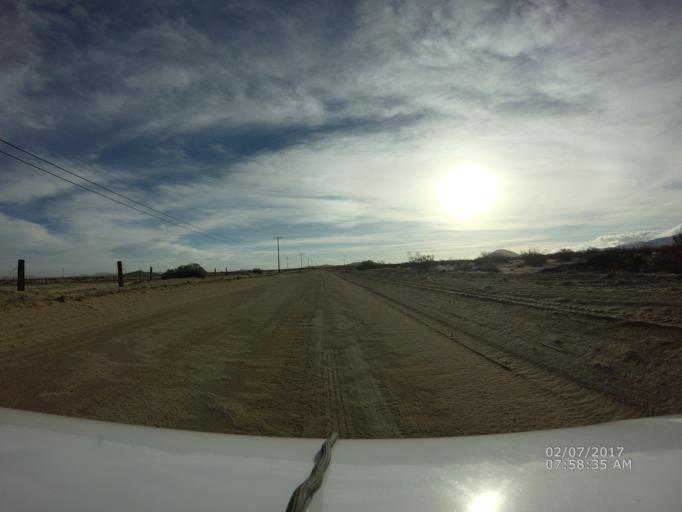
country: US
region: California
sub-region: Los Angeles County
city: Lake Los Angeles
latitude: 34.5873
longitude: -117.7765
